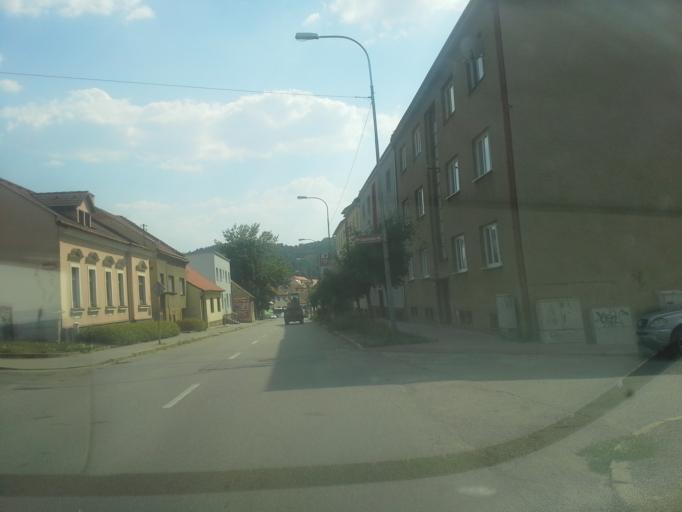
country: CZ
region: South Moravian
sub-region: Okres Blansko
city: Boskovice
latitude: 49.4922
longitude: 16.6627
